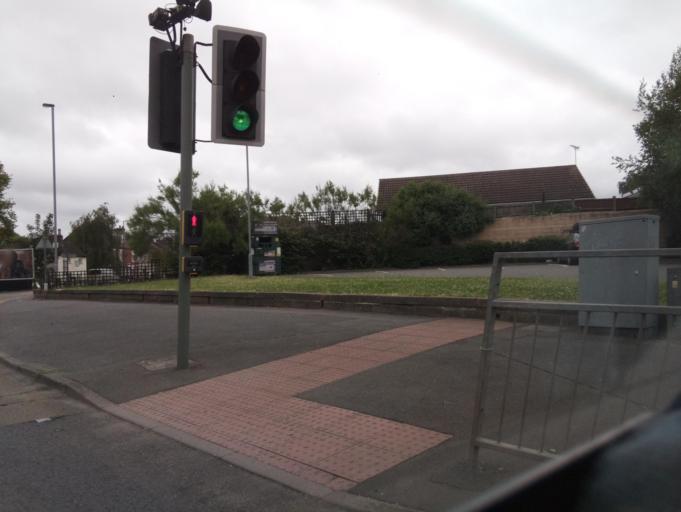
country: GB
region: England
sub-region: Staffordshire
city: Burton upon Trent
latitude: 52.8242
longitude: -1.6476
